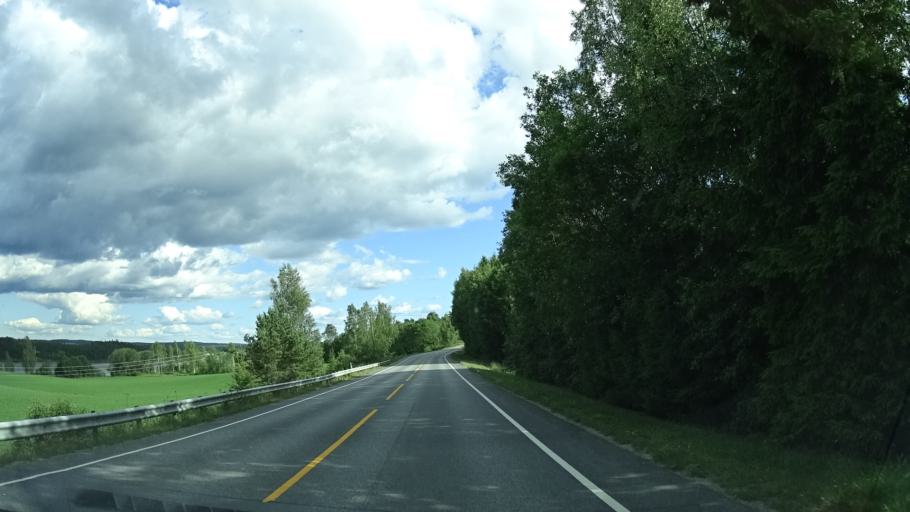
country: NO
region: Ostfold
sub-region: Marker
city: Orje
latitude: 59.4944
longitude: 11.6361
